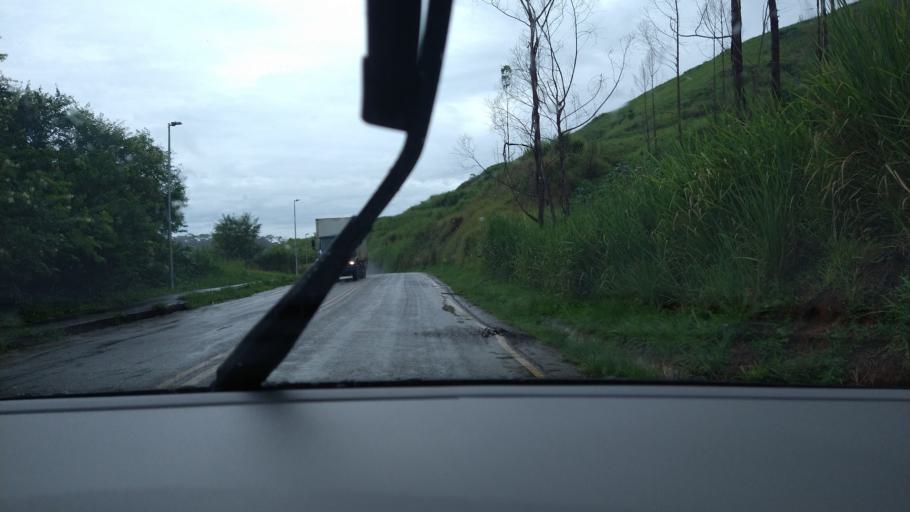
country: BR
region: Minas Gerais
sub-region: Ponte Nova
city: Ponte Nova
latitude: -20.3881
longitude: -42.9009
